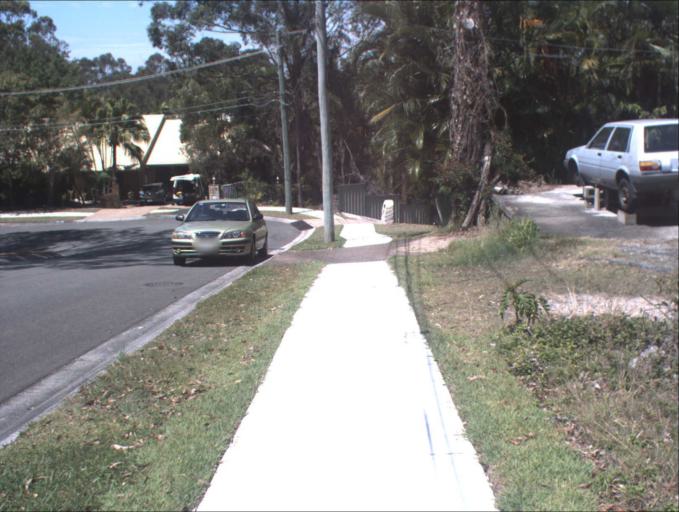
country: AU
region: Queensland
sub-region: Logan
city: Slacks Creek
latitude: -27.6309
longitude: 153.1498
